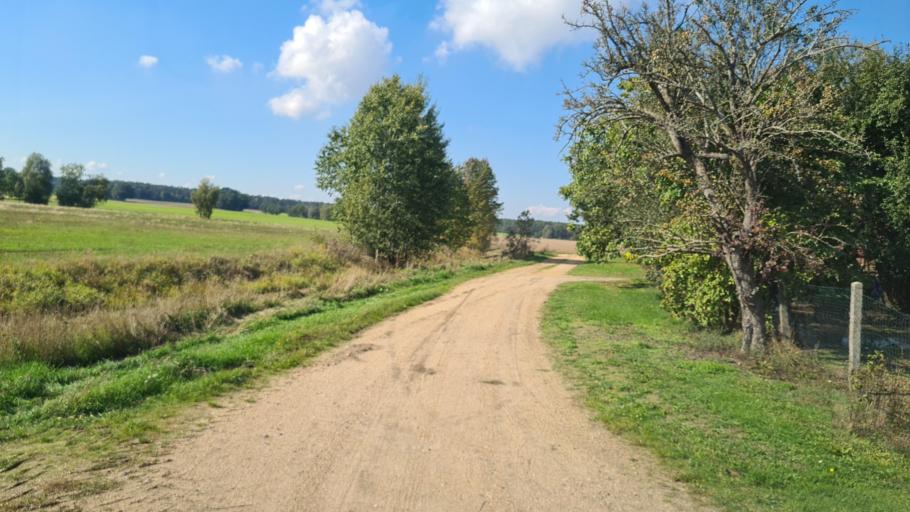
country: DE
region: Brandenburg
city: Lebusa
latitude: 51.8207
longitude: 13.4605
